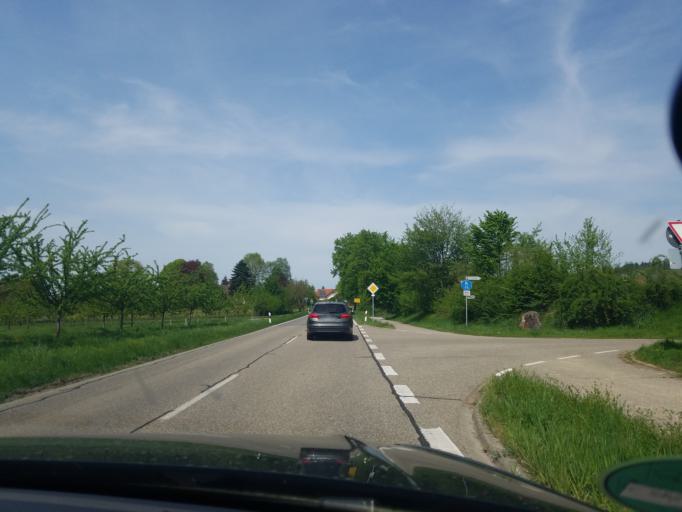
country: DE
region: Baden-Wuerttemberg
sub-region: Freiburg Region
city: Haslach
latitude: 48.5607
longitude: 8.0599
